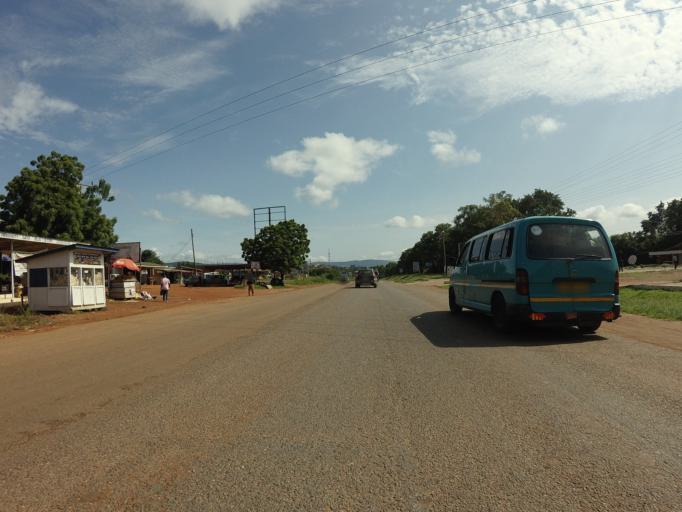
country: GH
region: Eastern
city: Aburi
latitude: 5.7992
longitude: -0.1272
